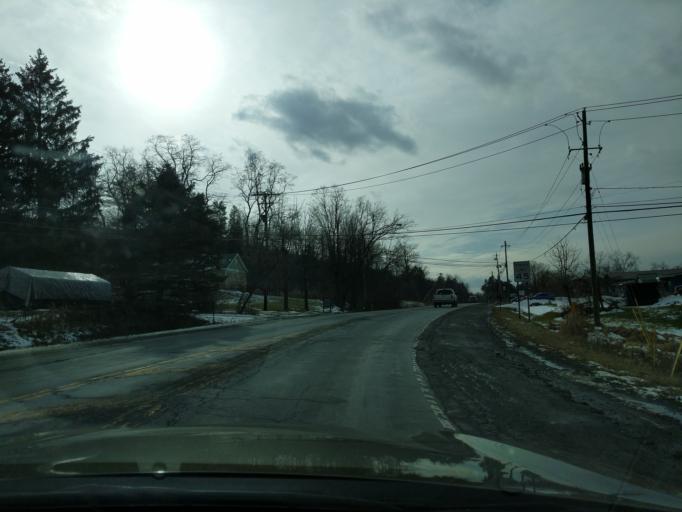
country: US
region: New York
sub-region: Tompkins County
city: Northeast Ithaca
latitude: 42.4682
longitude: -76.4094
